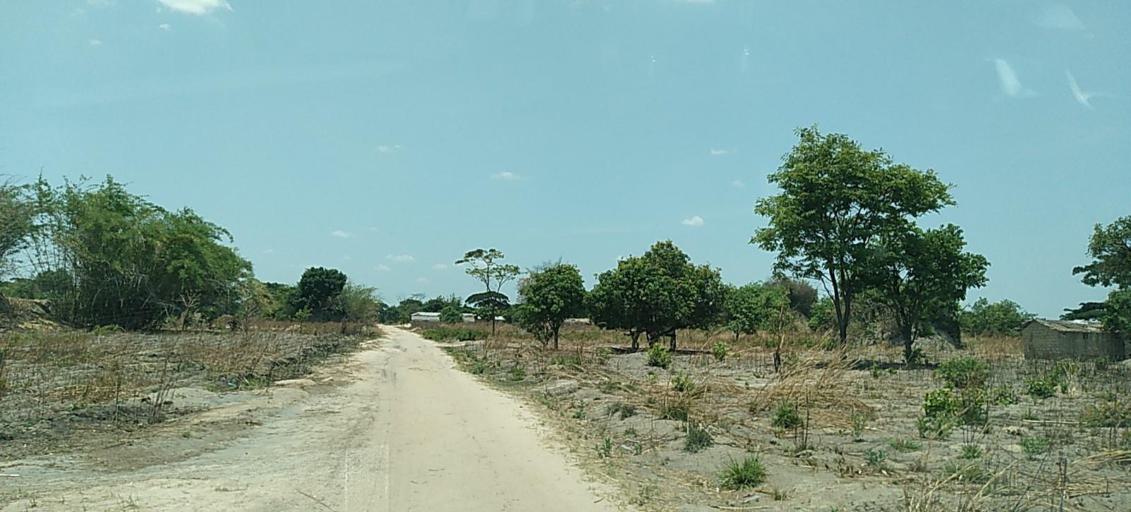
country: ZM
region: Copperbelt
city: Luanshya
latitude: -13.0753
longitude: 28.4049
